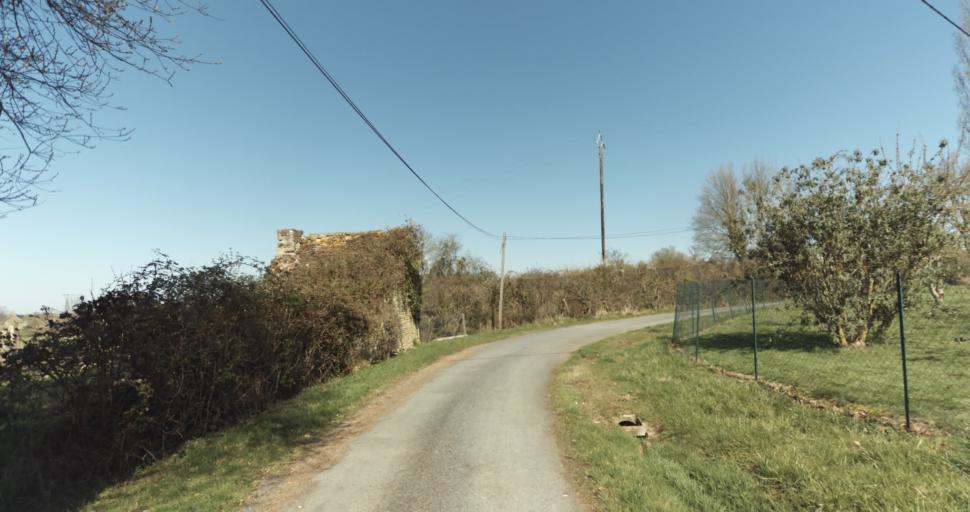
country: FR
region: Lower Normandy
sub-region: Departement du Calvados
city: Saint-Pierre-sur-Dives
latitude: 48.9605
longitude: -0.0011
